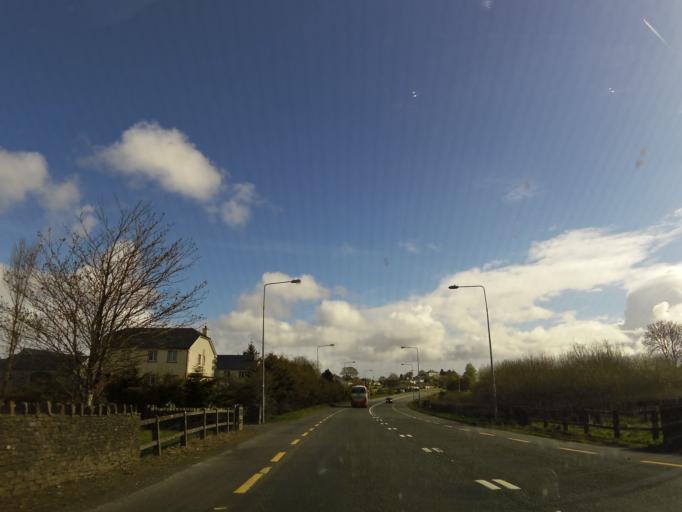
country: IE
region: Connaught
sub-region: Maigh Eo
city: Swinford
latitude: 53.8709
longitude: -8.8471
